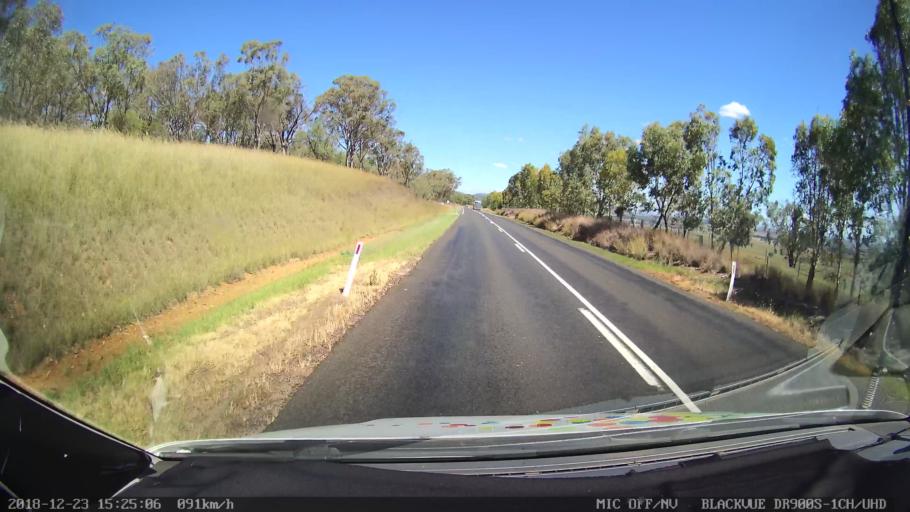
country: AU
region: New South Wales
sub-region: Tamworth Municipality
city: Manilla
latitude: -30.9002
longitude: 150.8275
